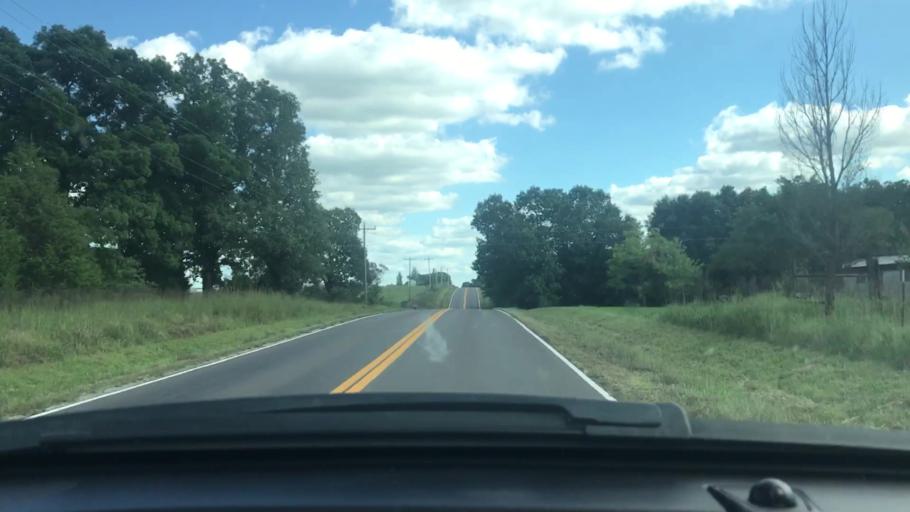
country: US
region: Missouri
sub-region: Wright County
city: Mountain Grove
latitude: 37.3111
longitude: -92.3171
